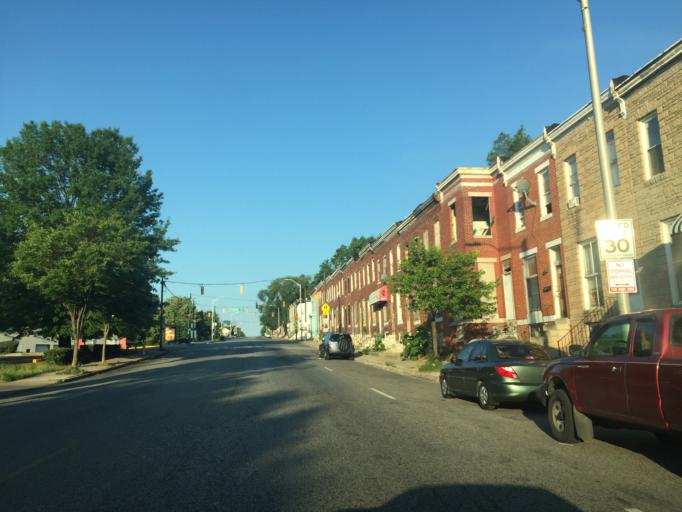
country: US
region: Maryland
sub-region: Baltimore County
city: Lansdowne
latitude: 39.2841
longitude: -76.6548
